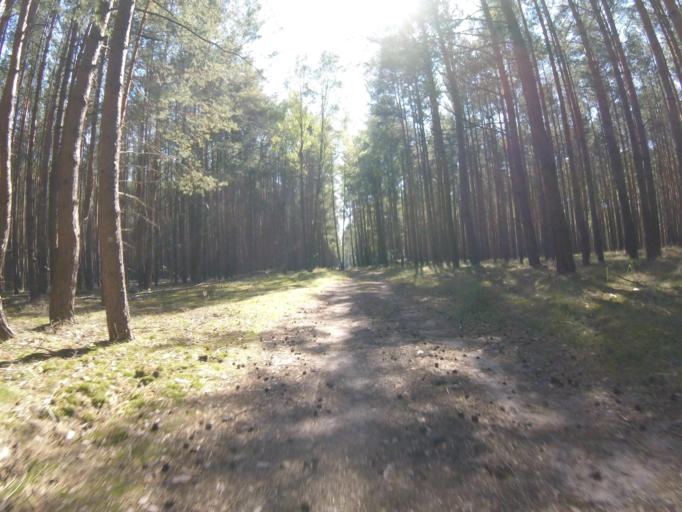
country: DE
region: Brandenburg
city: Bestensee
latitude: 52.2634
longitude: 13.6766
